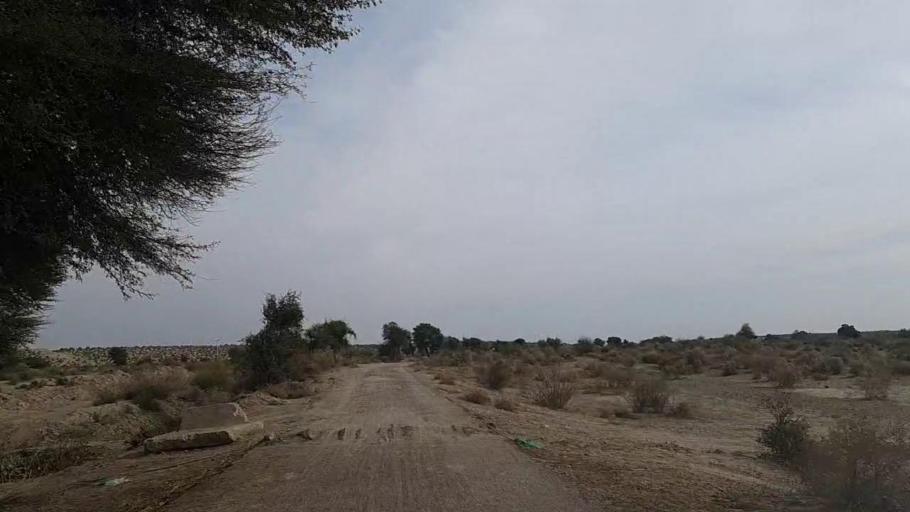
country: PK
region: Sindh
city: Jam Sahib
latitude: 26.4455
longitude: 68.6199
